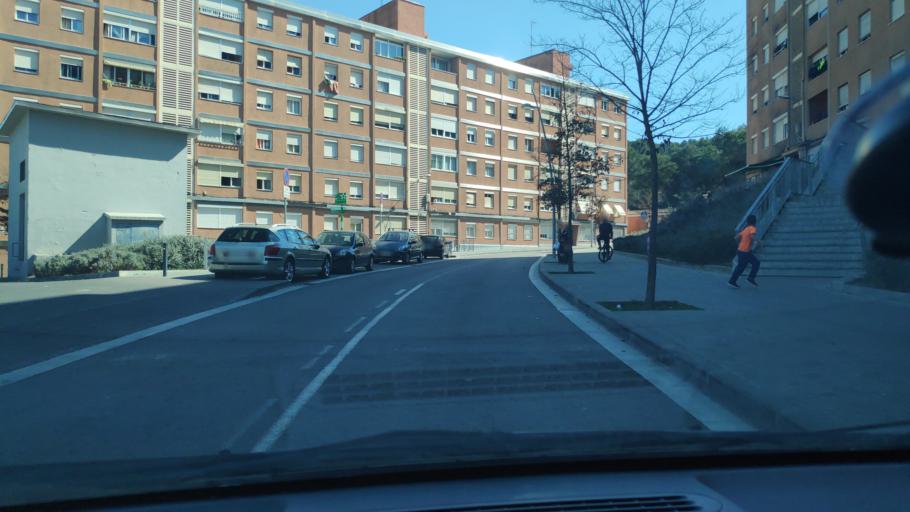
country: ES
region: Catalonia
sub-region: Provincia de Barcelona
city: Rubi
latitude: 41.5087
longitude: 2.0472
